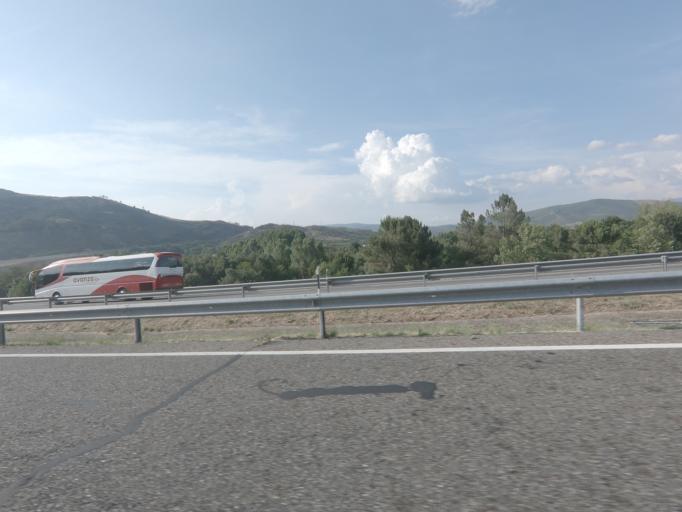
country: ES
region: Galicia
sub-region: Provincia de Ourense
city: Oimbra
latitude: 41.9256
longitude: -7.4950
